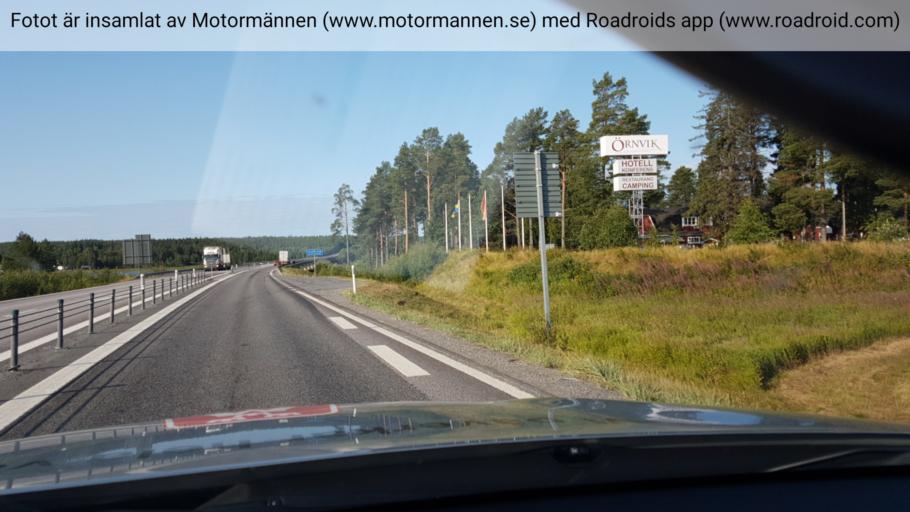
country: SE
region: Norrbotten
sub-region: Lulea Kommun
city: Gammelstad
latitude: 65.5938
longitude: 22.0372
